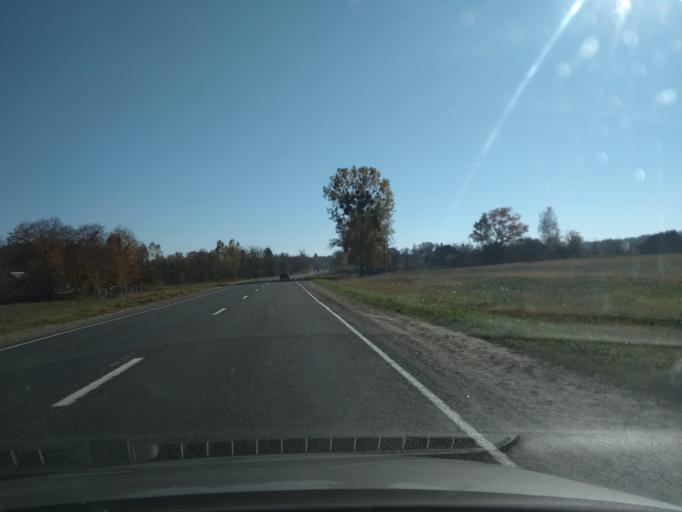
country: BY
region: Brest
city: Malaryta
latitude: 51.9279
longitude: 24.0676
